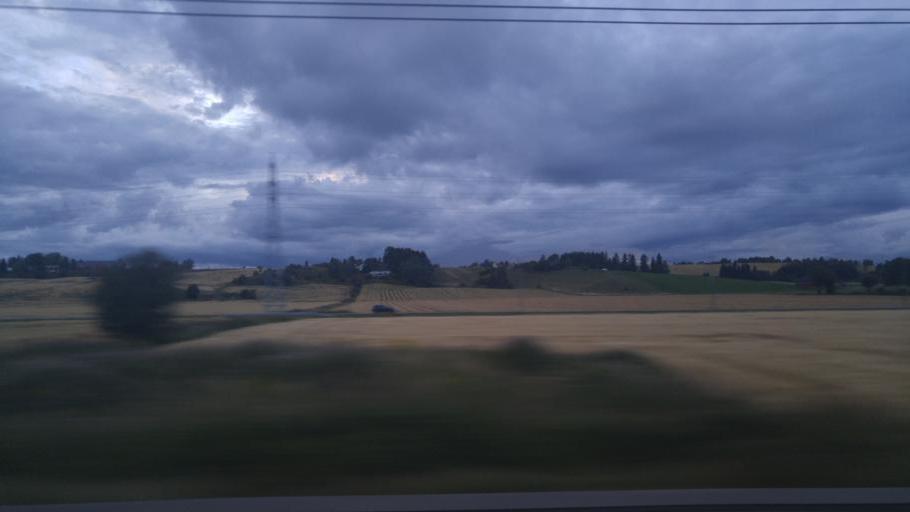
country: NO
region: Akershus
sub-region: Skedsmo
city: Leirsund
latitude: 59.9765
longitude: 11.0708
